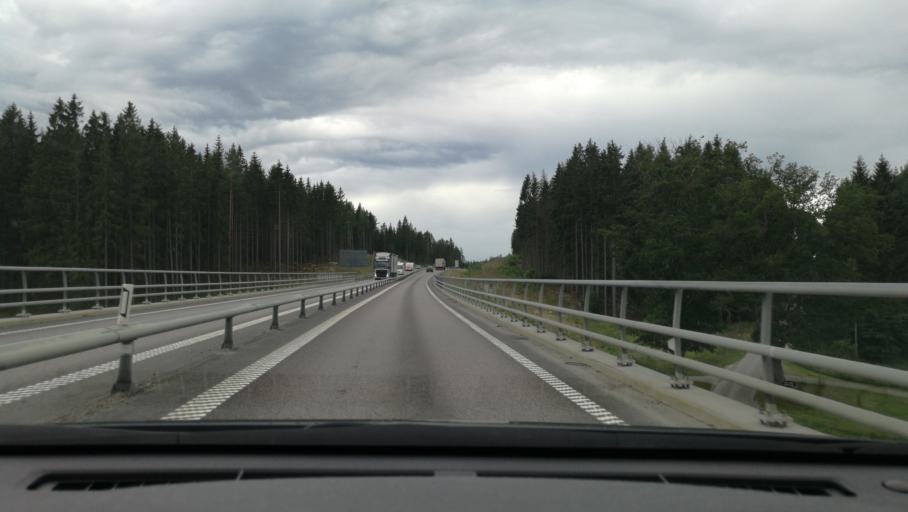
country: SE
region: Soedermanland
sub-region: Katrineholms Kommun
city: Katrineholm
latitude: 58.9696
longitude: 16.2586
